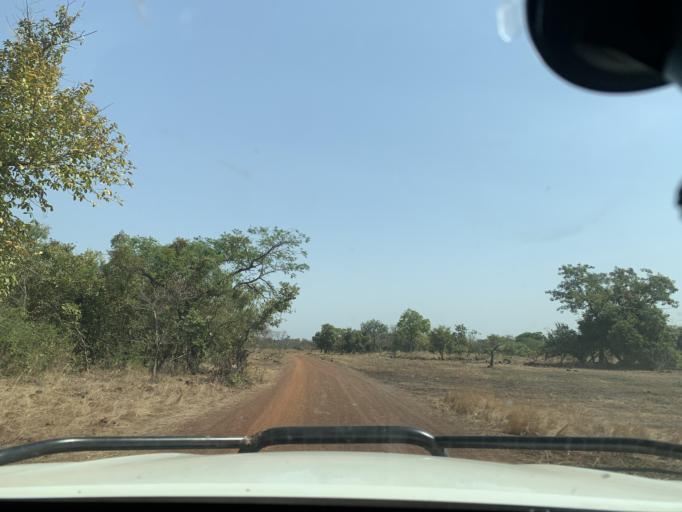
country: ML
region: Sikasso
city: Kolondieba
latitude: 10.8343
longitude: -6.7882
